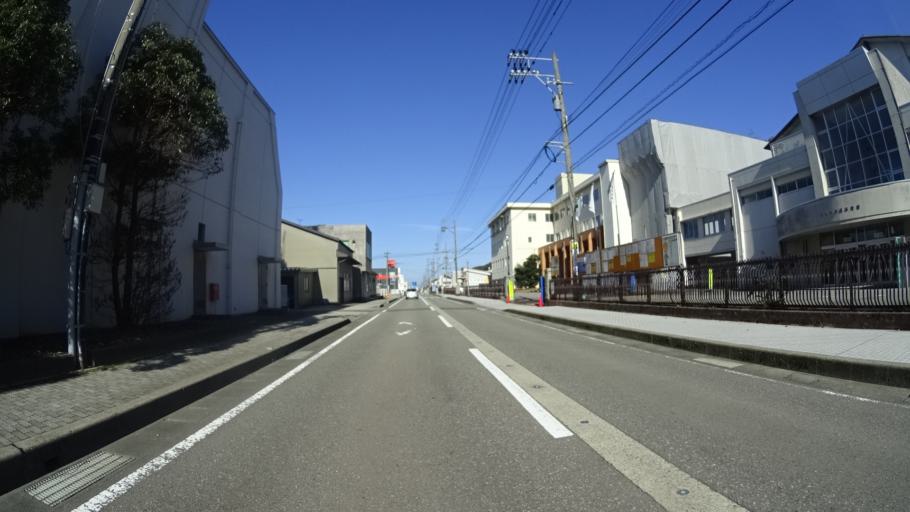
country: JP
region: Ishikawa
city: Tsurugi-asahimachi
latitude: 36.4537
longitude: 136.6245
